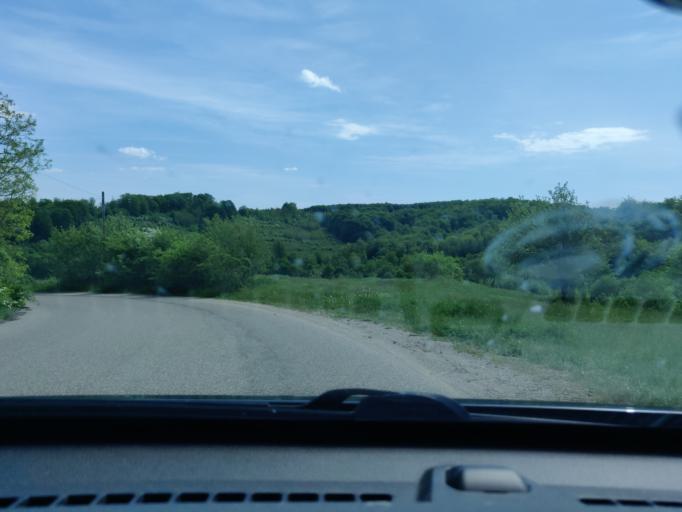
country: RO
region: Vrancea
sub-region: Comuna Campuri
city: Campuri
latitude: 45.9989
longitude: 26.7903
